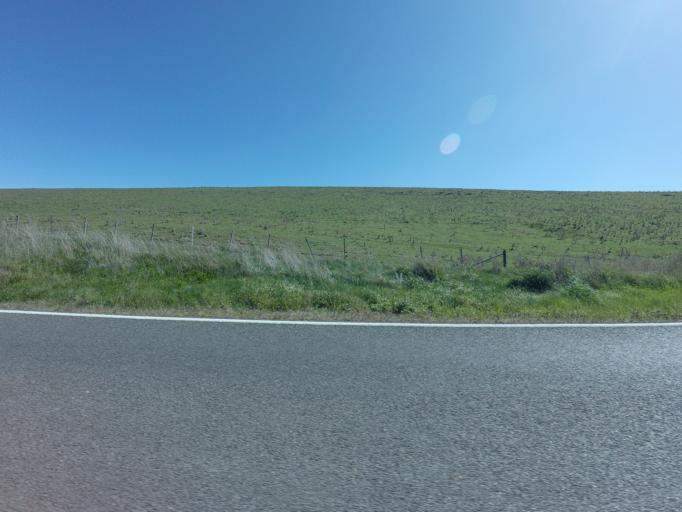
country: AU
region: Tasmania
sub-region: Derwent Valley
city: New Norfolk
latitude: -42.6386
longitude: 146.9179
